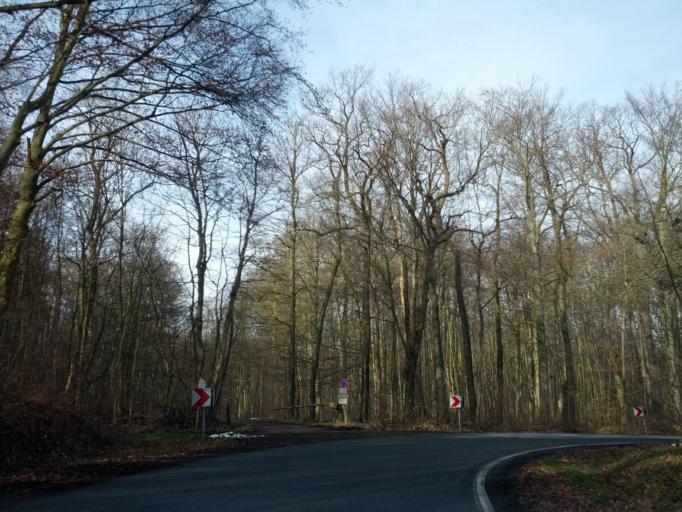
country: DE
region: Thuringia
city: Weberstedt
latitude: 51.0807
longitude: 10.5133
